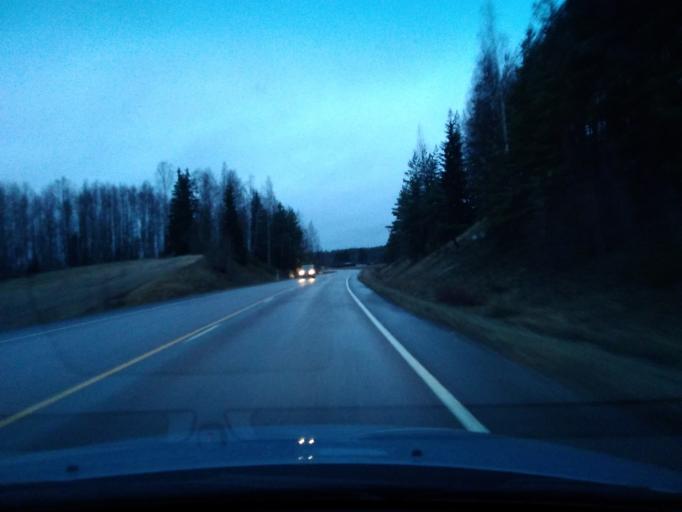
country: FI
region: Uusimaa
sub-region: Porvoo
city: Askola
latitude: 60.4710
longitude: 25.5694
